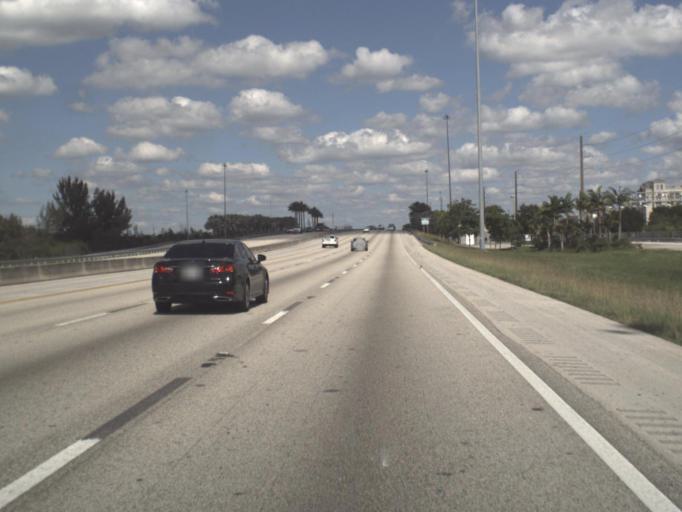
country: US
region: Florida
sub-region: Miami-Dade County
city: Doral
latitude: 25.8076
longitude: -80.3861
